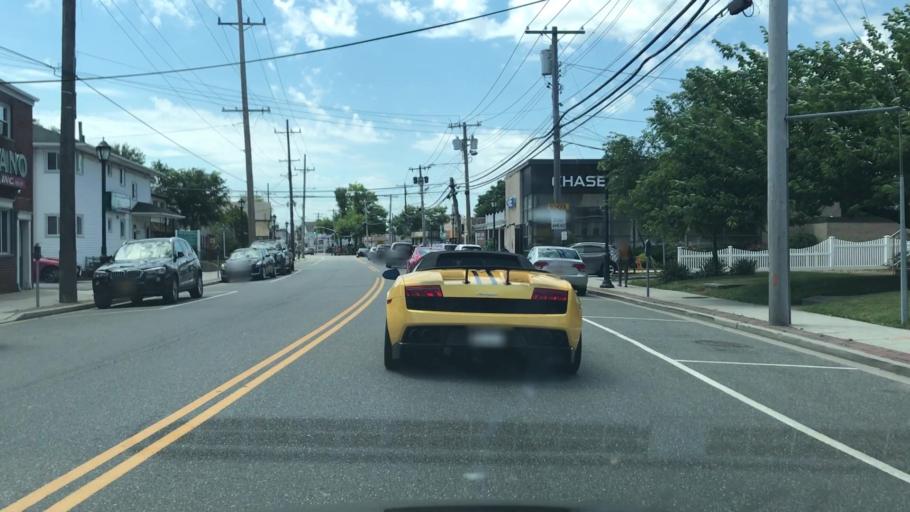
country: US
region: New York
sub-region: Nassau County
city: Valley Stream
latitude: 40.6756
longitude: -73.7095
